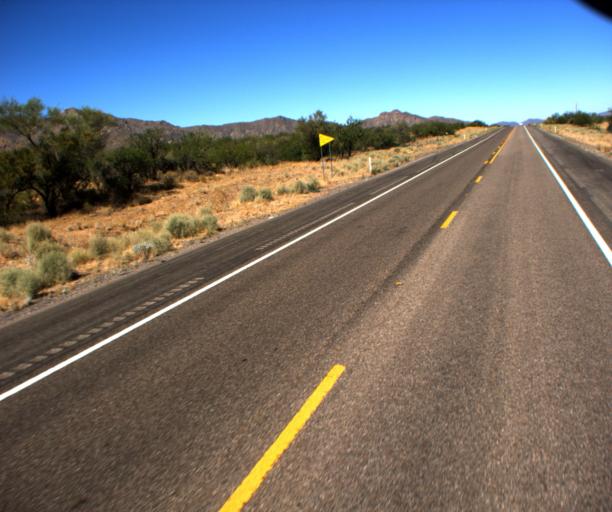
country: US
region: Arizona
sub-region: Pima County
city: Sells
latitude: 32.0212
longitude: -111.6065
